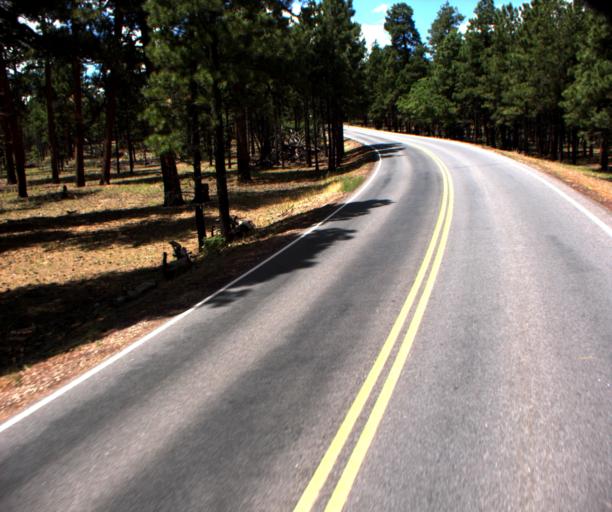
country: US
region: Arizona
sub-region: Coconino County
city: Grand Canyon
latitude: 35.9757
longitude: -111.9830
